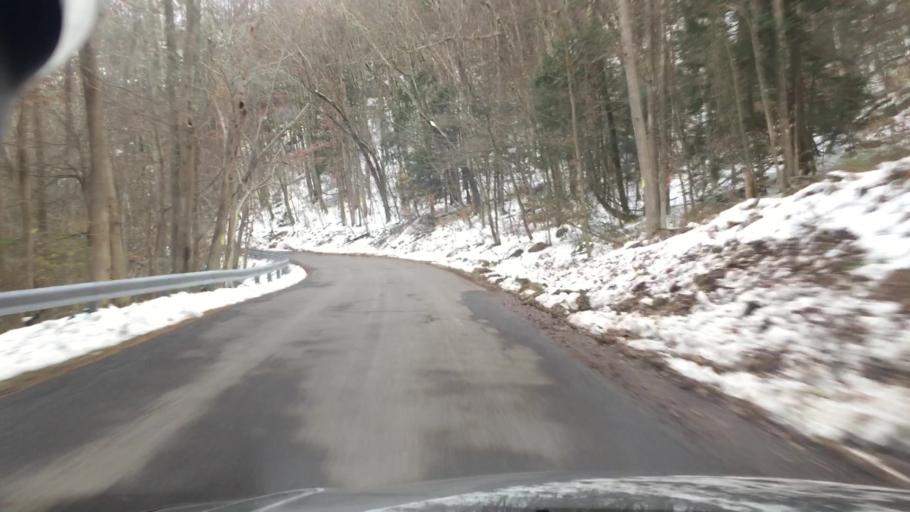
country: US
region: Pennsylvania
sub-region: Luzerne County
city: Conyngham
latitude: 41.0121
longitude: -76.1006
